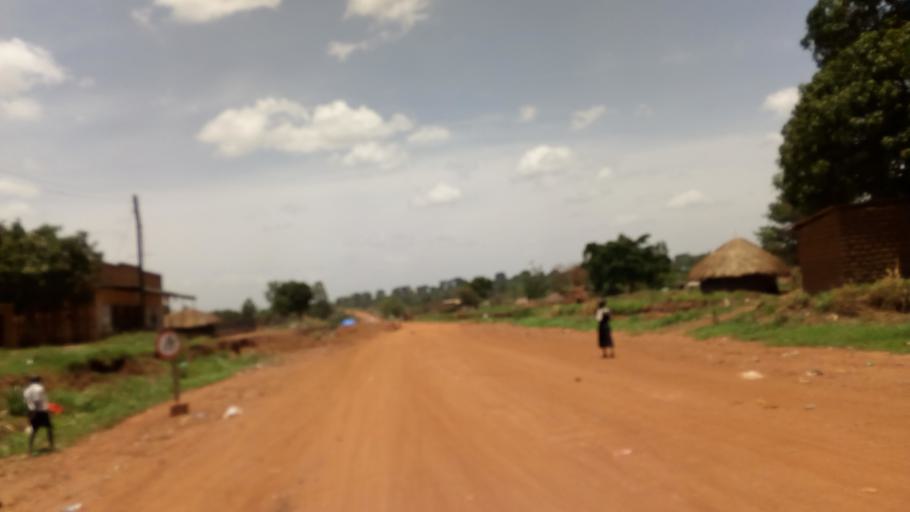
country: UG
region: Northern Region
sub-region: Gulu District
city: Gulu
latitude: 2.8165
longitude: 32.3372
